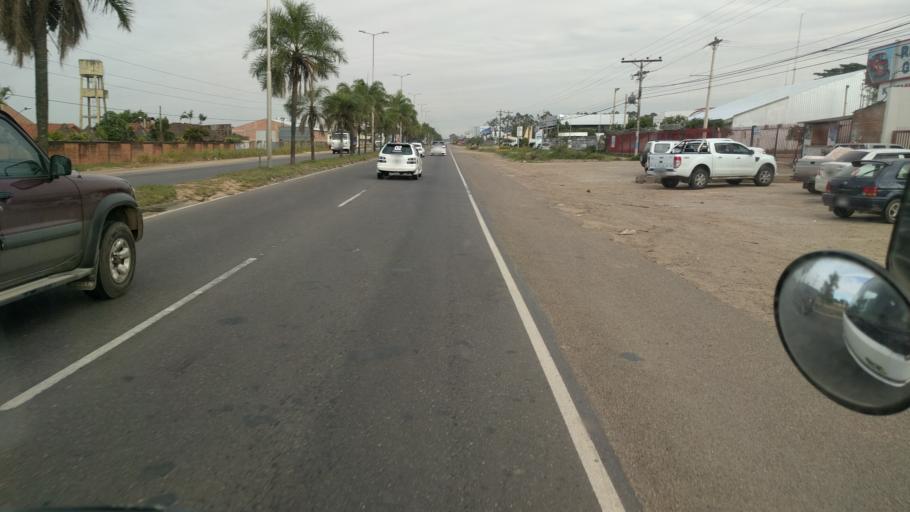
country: BO
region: Santa Cruz
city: Santa Cruz de la Sierra
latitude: -17.6877
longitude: -63.1592
